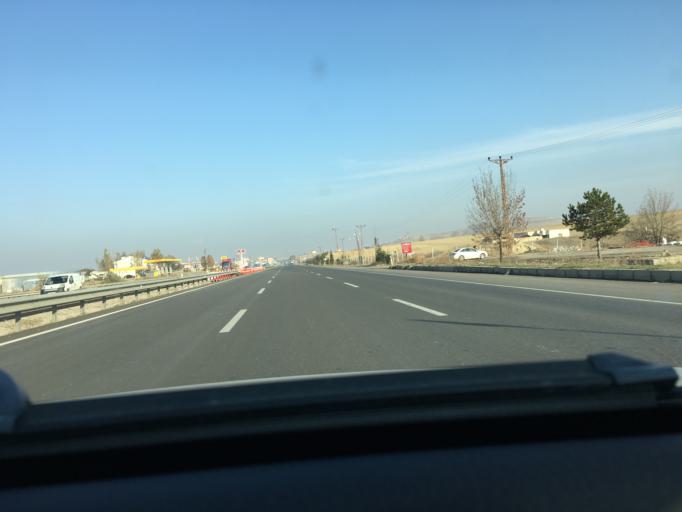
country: TR
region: Ankara
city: Temelli
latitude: 39.7195
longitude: 32.3270
